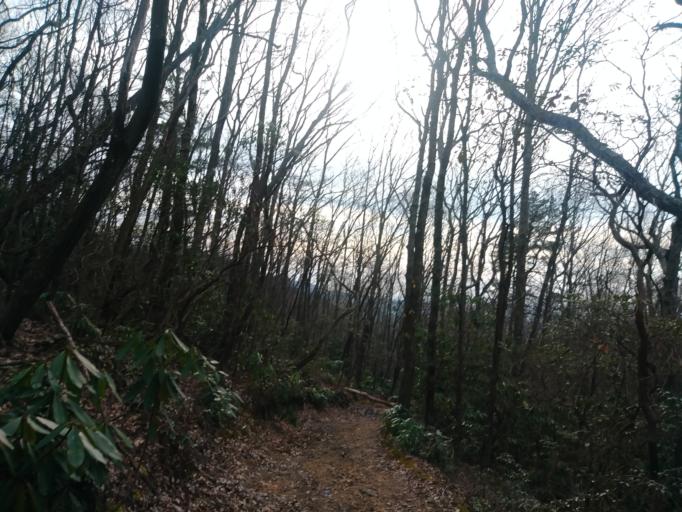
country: US
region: Tennessee
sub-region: Greene County
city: Tusculum
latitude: 36.0593
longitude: -82.6748
